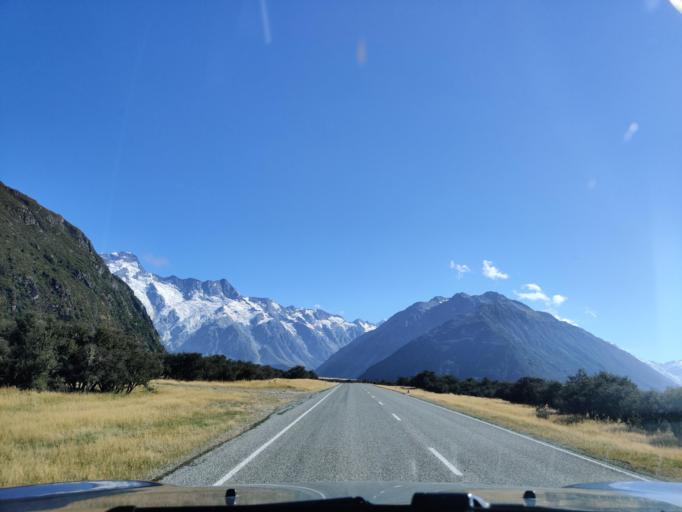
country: NZ
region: Canterbury
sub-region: Timaru District
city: Pleasant Point
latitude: -43.7636
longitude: 170.1224
